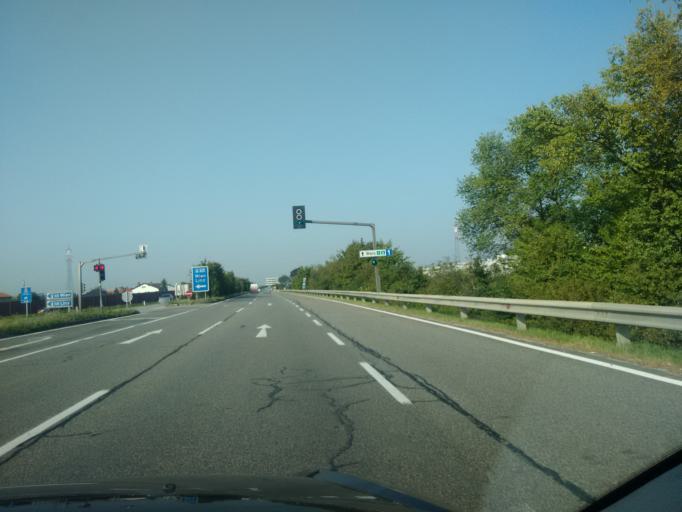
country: AT
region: Upper Austria
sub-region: Wels-Land
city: Marchtrenk
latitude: 48.1878
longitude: 14.0845
